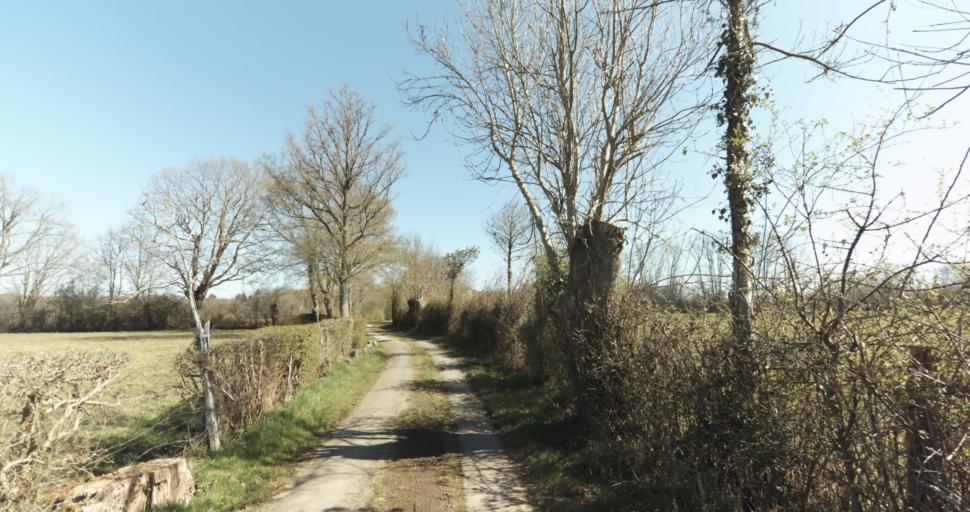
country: FR
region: Lower Normandy
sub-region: Departement du Calvados
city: Livarot
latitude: 49.0230
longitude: 0.1029
